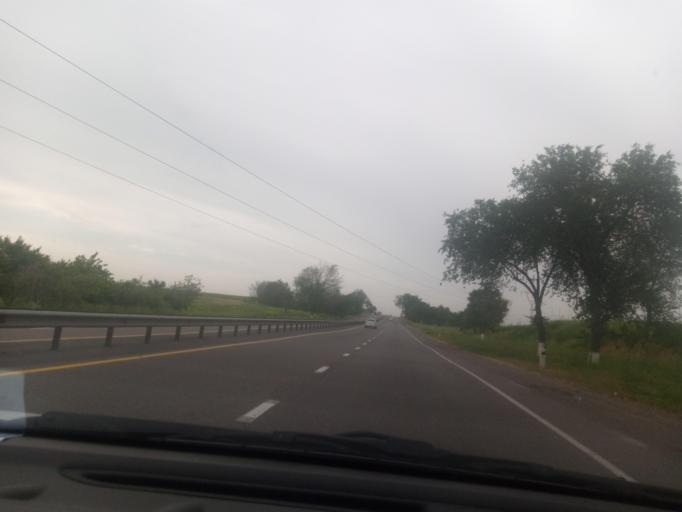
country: UZ
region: Toshkent
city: Tuytepa
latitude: 41.0680
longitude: 69.4789
